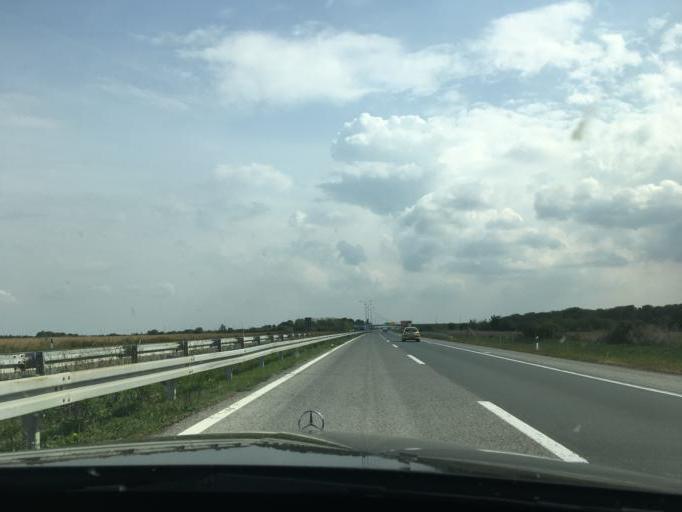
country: RS
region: Autonomna Pokrajina Vojvodina
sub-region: Sremski Okrug
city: Ruma
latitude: 44.9656
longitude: 19.7965
